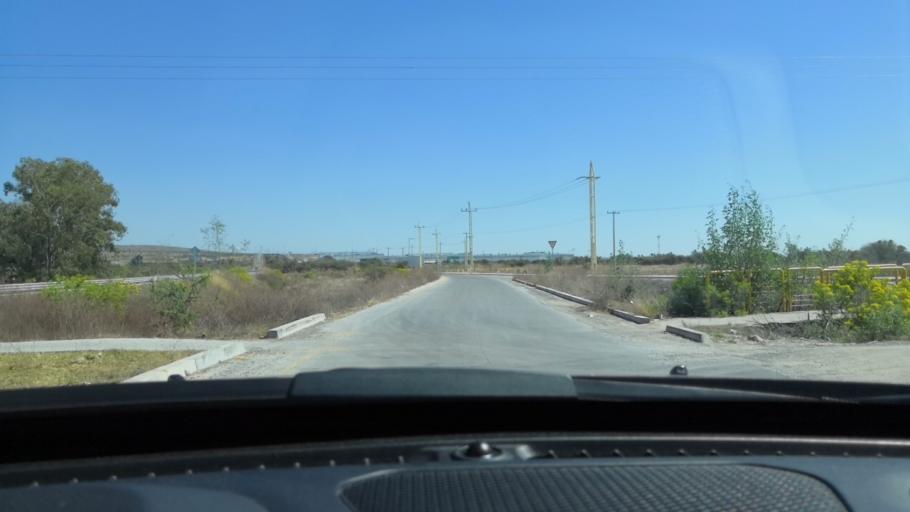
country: MX
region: Guanajuato
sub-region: Leon
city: Centro Familiar la Soledad
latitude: 21.1004
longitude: -101.7766
